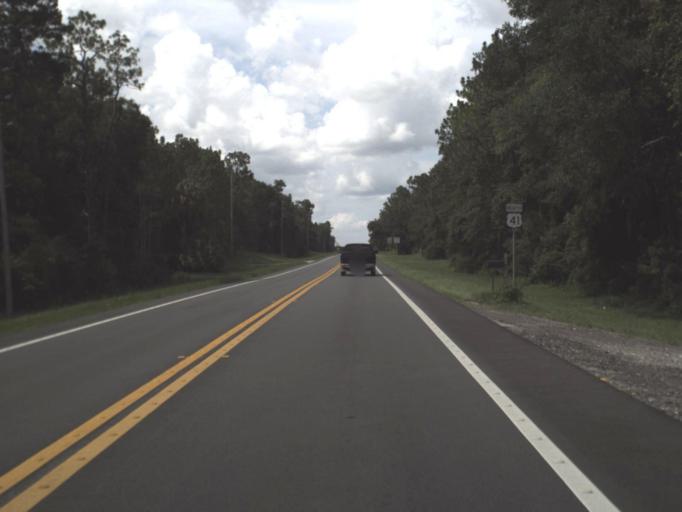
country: US
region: Florida
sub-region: Citrus County
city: Floral City
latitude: 28.6670
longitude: -82.3227
